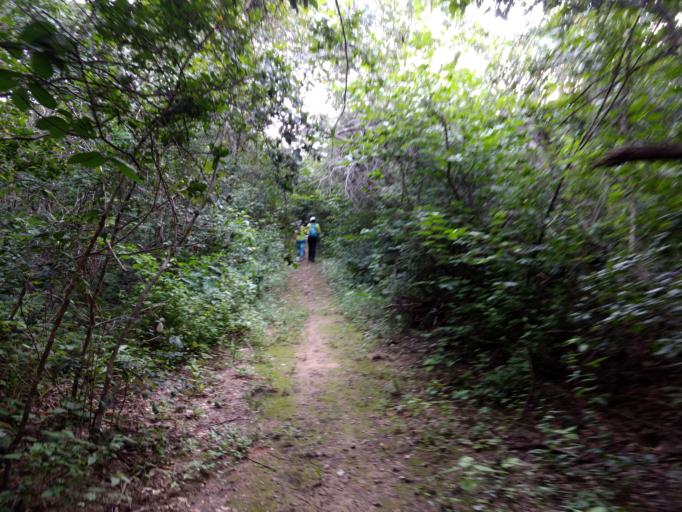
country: BR
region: Ceara
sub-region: Crateus
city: Crateus
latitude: -5.1423
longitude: -40.9202
